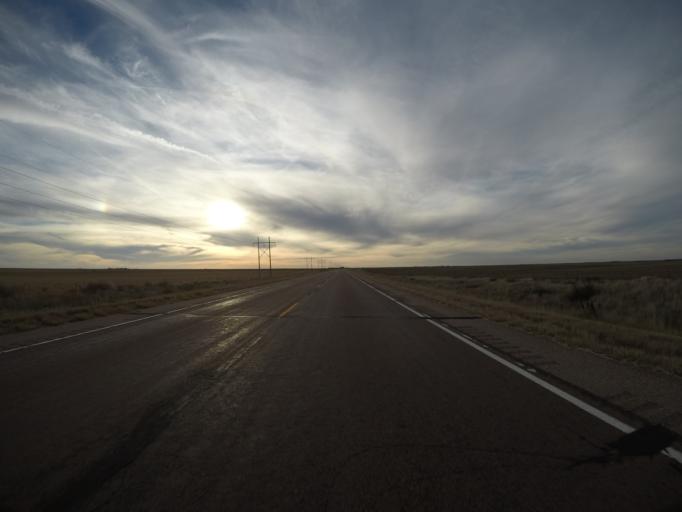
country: US
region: Colorado
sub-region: Yuma County
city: Yuma
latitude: 39.6549
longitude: -102.7970
